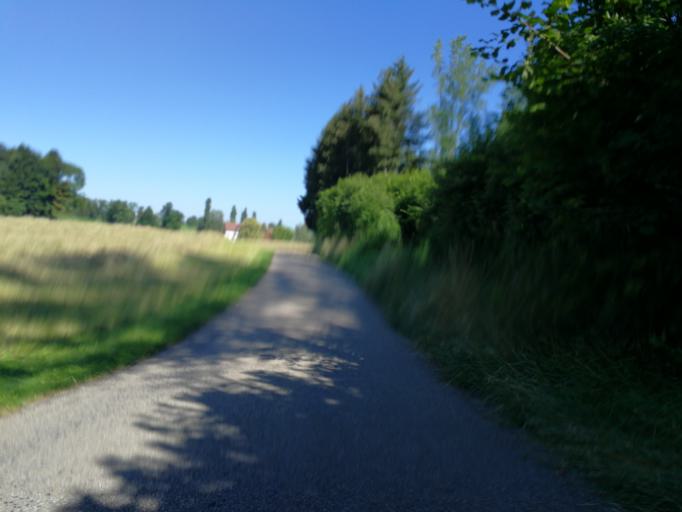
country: CH
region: Zurich
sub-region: Bezirk Hinwil
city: Durnten
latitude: 47.2841
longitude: 8.8376
